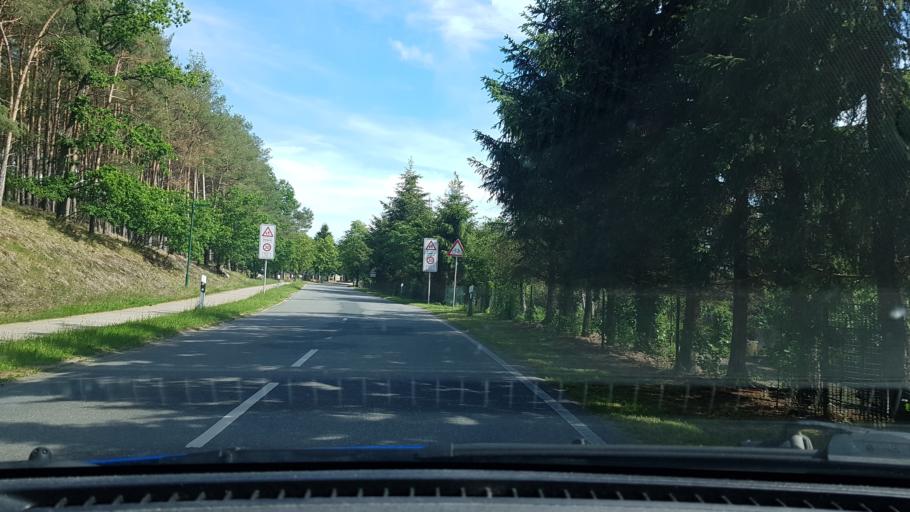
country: DE
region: Lower Saxony
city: Neu Darchau
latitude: 53.2916
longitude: 10.9288
